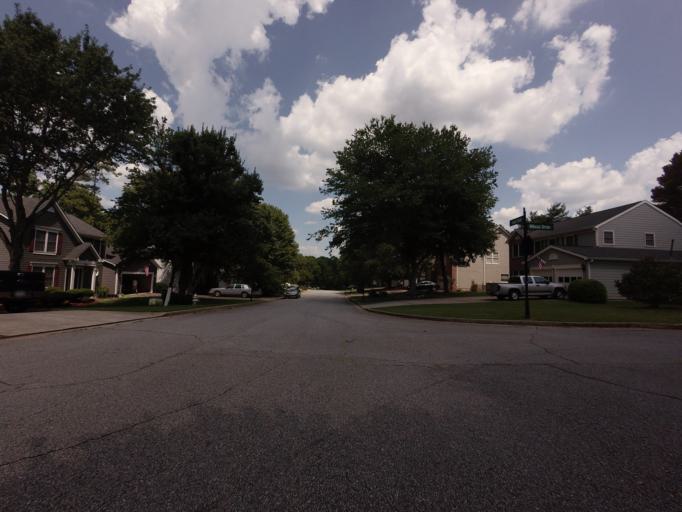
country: US
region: Georgia
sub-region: Fulton County
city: Johns Creek
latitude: 34.0476
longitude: -84.2042
